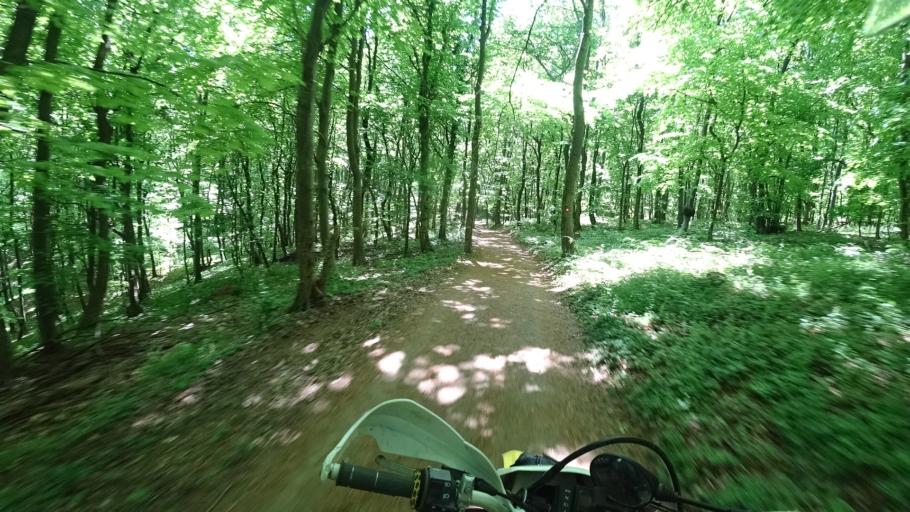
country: HR
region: Zagrebacka
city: Jablanovec
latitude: 45.8619
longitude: 15.8674
